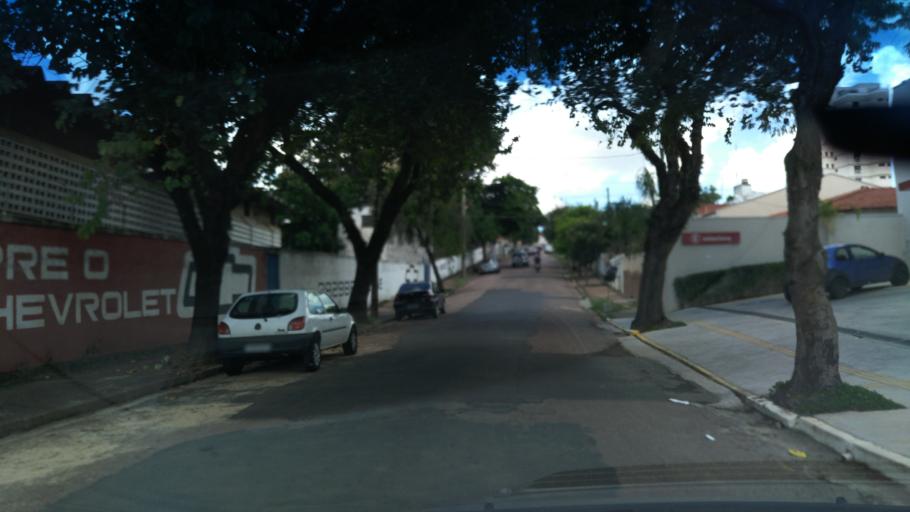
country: BR
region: Sao Paulo
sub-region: Valinhos
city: Valinhos
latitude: -22.9638
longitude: -47.0038
